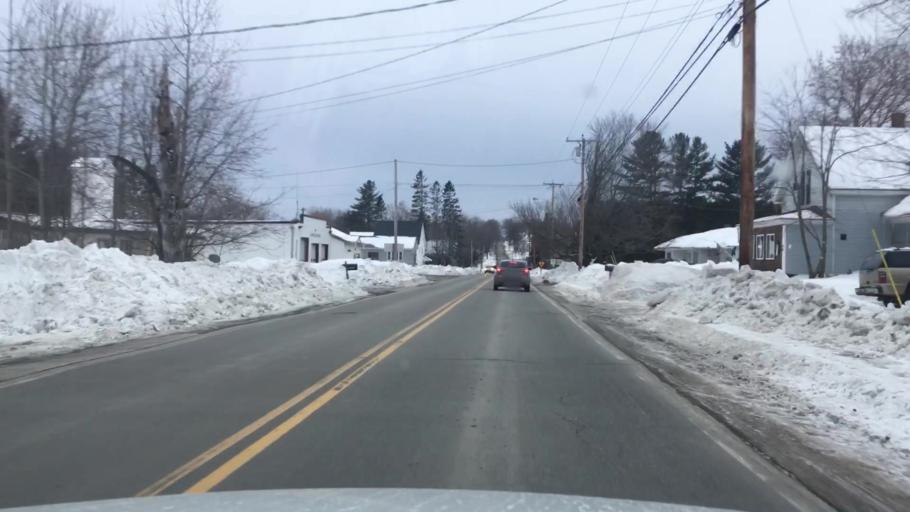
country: US
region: Maine
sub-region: Penobscot County
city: Corinna
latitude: 44.9232
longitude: -69.2557
